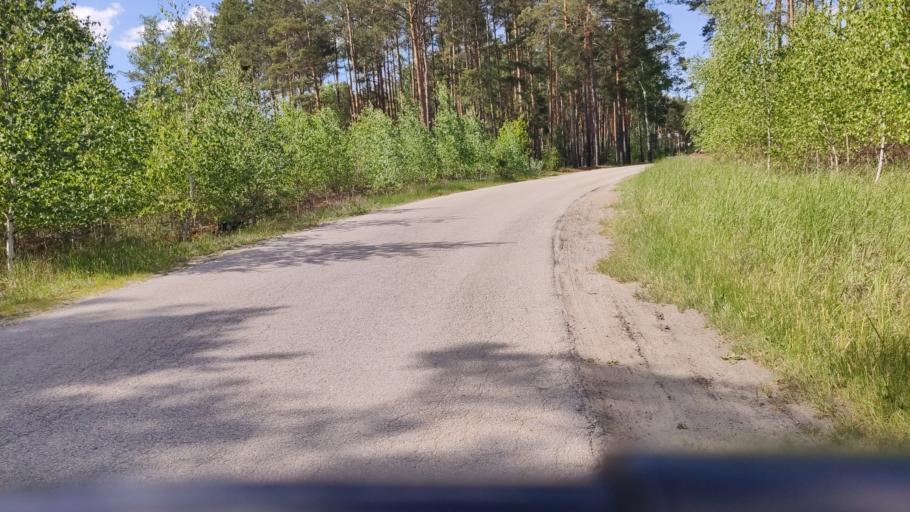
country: PL
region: Kujawsko-Pomorskie
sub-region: Wloclawek
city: Wloclawek
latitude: 52.5997
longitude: 19.0811
